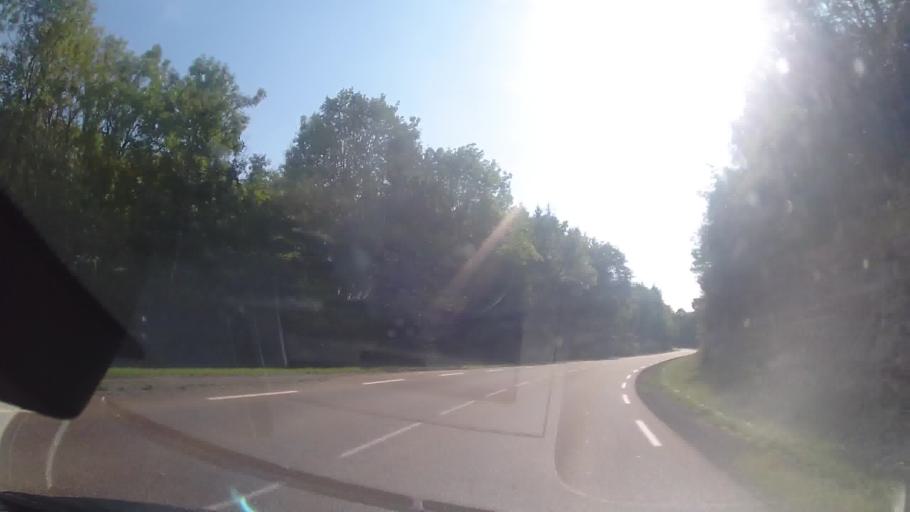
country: FR
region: Franche-Comte
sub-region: Departement du Jura
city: Clairvaux-les-Lacs
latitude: 46.5973
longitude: 5.8469
